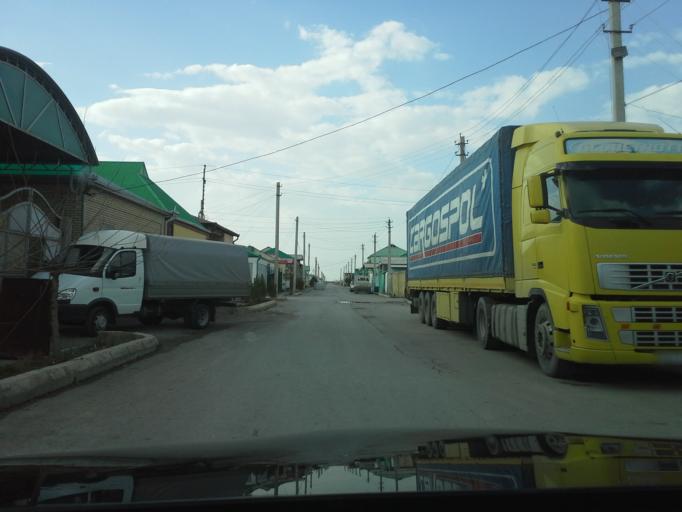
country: TM
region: Ahal
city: Ashgabat
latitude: 37.9905
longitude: 58.2941
